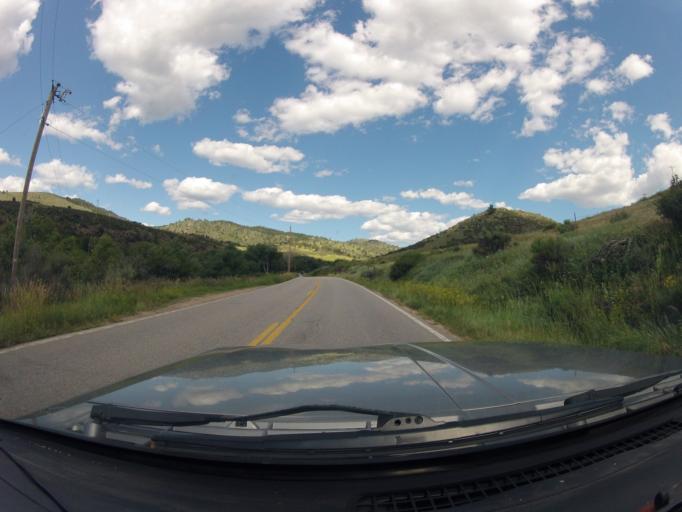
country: US
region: Colorado
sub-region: Larimer County
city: Laporte
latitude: 40.5375
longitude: -105.2744
